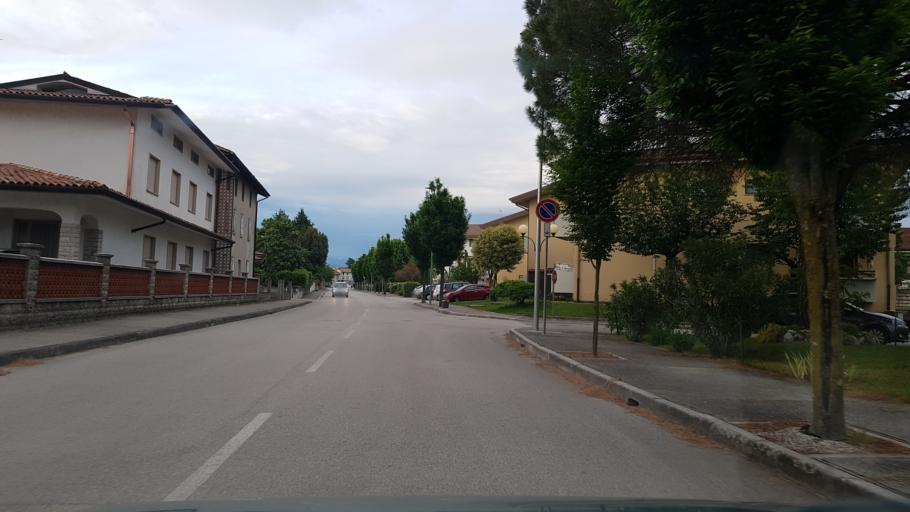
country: IT
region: Friuli Venezia Giulia
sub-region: Provincia di Gorizia
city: Farra d'Isonzo
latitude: 45.9081
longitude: 13.5141
